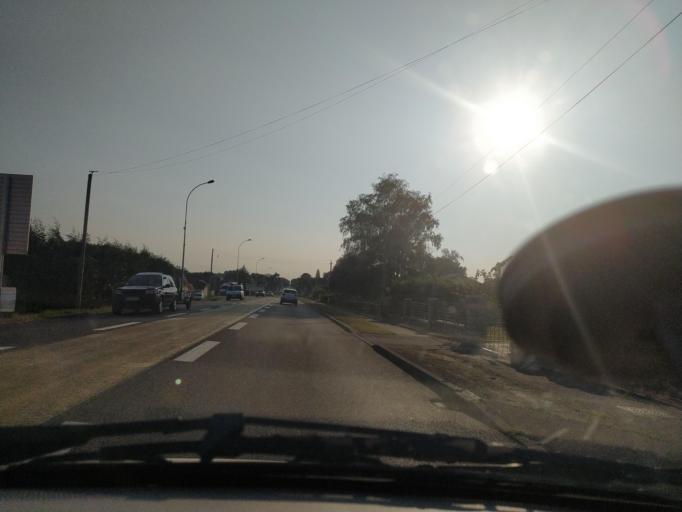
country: FR
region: Aquitaine
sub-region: Departement des Landes
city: Saint-Geours-de-Maremne
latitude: 43.6867
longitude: -1.2322
